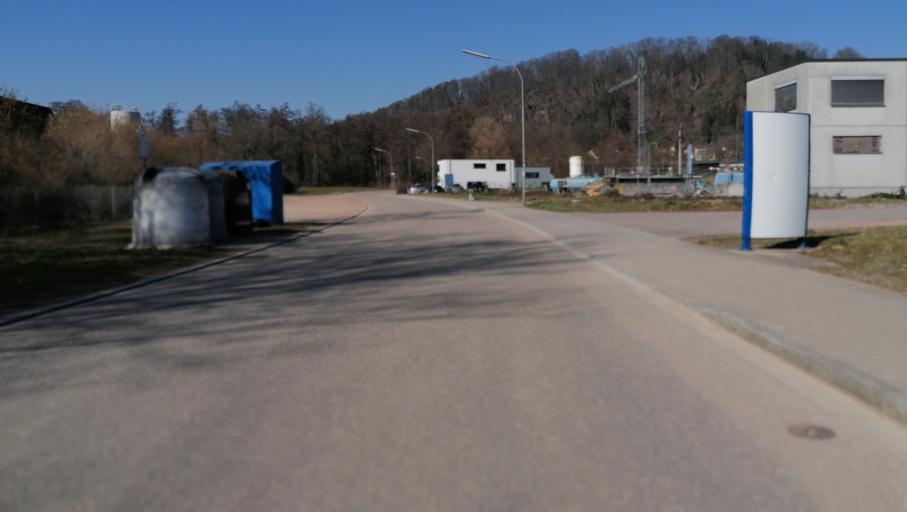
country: DE
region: Baden-Wuerttemberg
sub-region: Freiburg Region
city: Schworstadt
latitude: 47.5818
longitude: 7.9075
